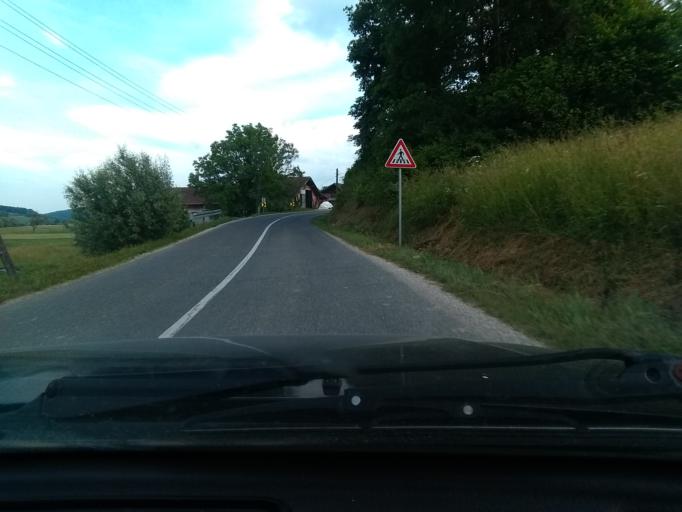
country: HR
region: Krapinsko-Zagorska
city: Pregrada
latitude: 46.0792
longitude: 15.7481
